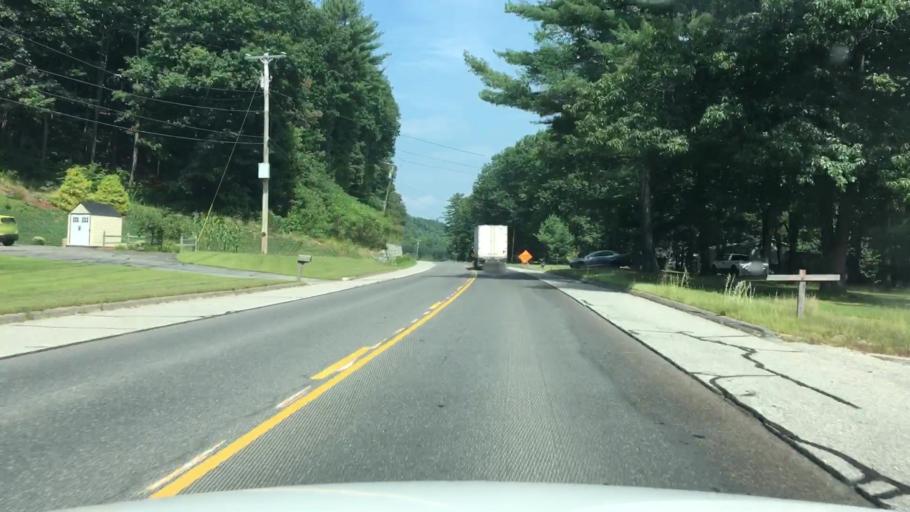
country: US
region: Maine
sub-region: Androscoggin County
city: Turner
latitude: 44.3071
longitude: -70.2662
